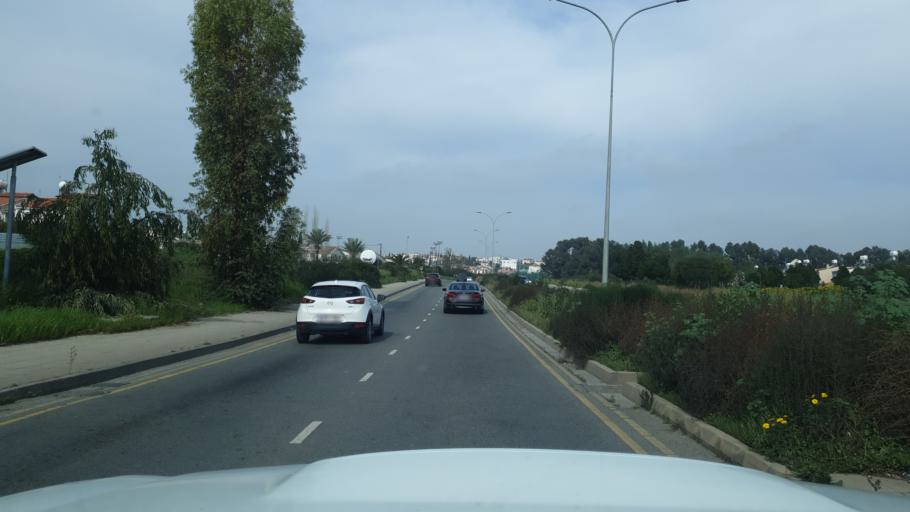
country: CY
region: Lefkosia
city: Tseri
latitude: 35.1306
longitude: 33.3154
